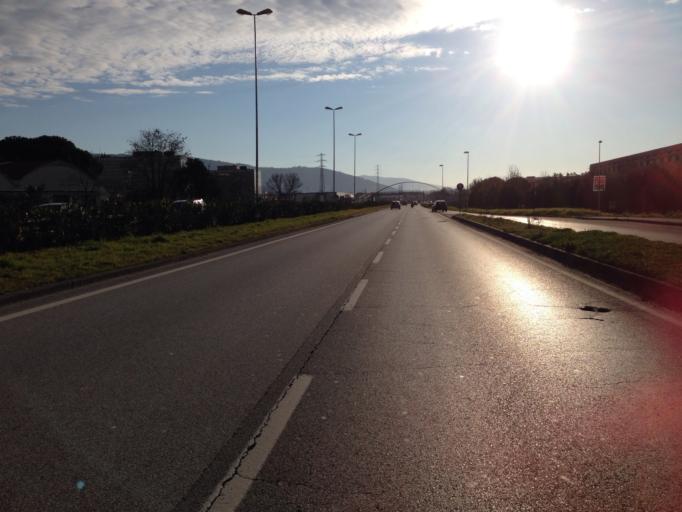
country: IT
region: Tuscany
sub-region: Provincia di Prato
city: Prato
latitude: 43.8780
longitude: 11.0677
